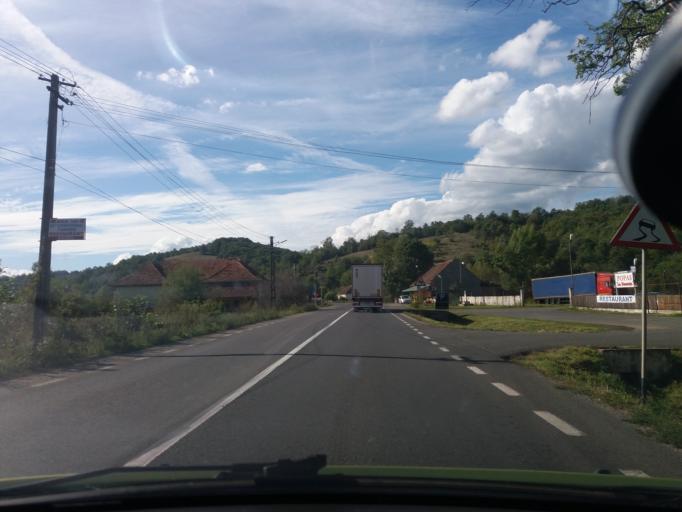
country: RO
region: Arad
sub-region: Comuna Petris
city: Petris
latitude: 46.0150
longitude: 22.3611
